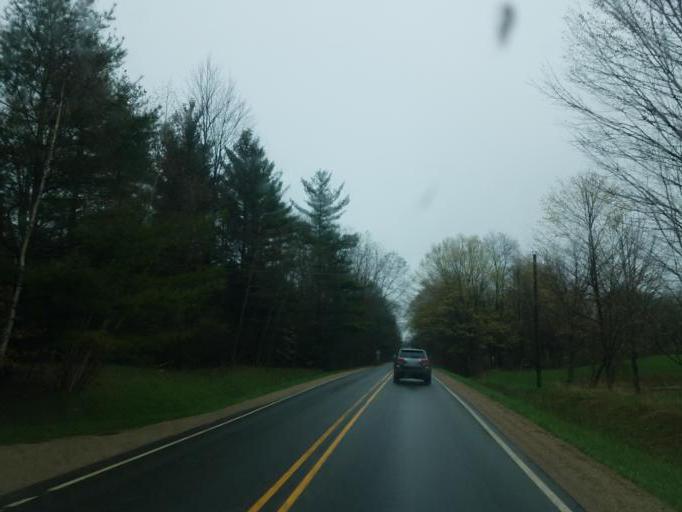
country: US
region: Michigan
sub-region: Montcalm County
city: Edmore
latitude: 43.5238
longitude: -85.0244
